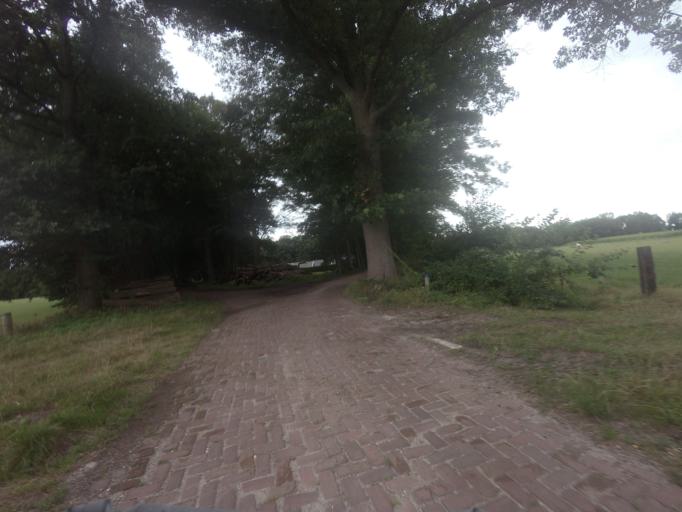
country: NL
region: Overijssel
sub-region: Gemeente Raalte
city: Raalte
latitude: 52.3226
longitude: 6.2876
